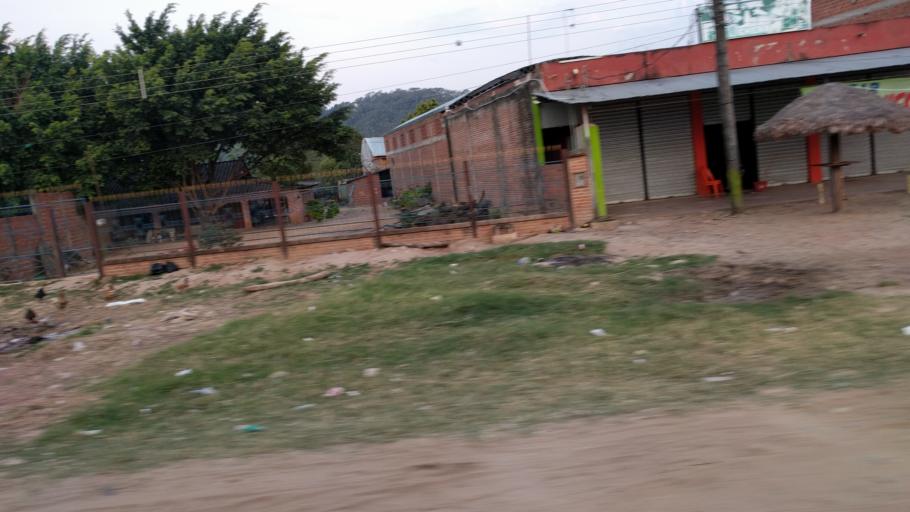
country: BO
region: Santa Cruz
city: Santiago del Torno
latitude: -17.9874
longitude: -63.3779
